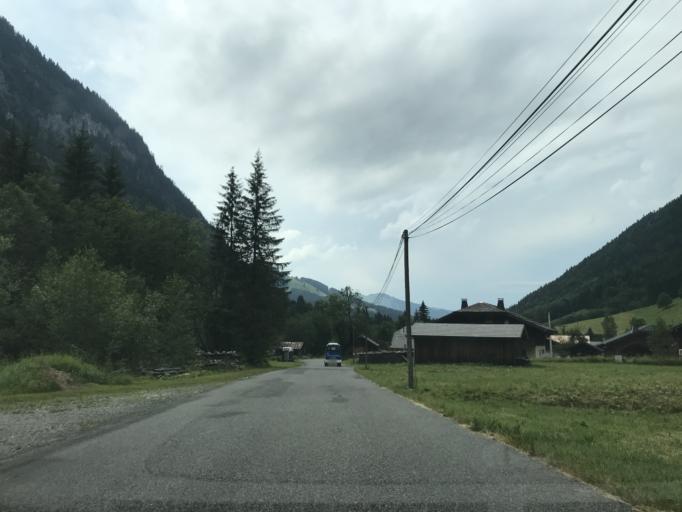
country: FR
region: Rhone-Alpes
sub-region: Departement de la Haute-Savoie
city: Morzine
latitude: 46.1560
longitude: 6.7339
